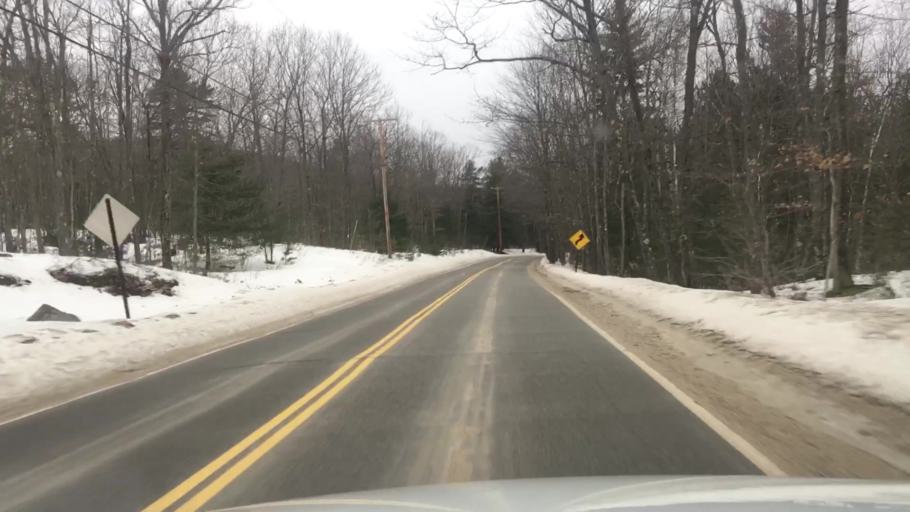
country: US
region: Maine
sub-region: York County
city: Newfield
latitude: 43.6302
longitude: -70.8401
